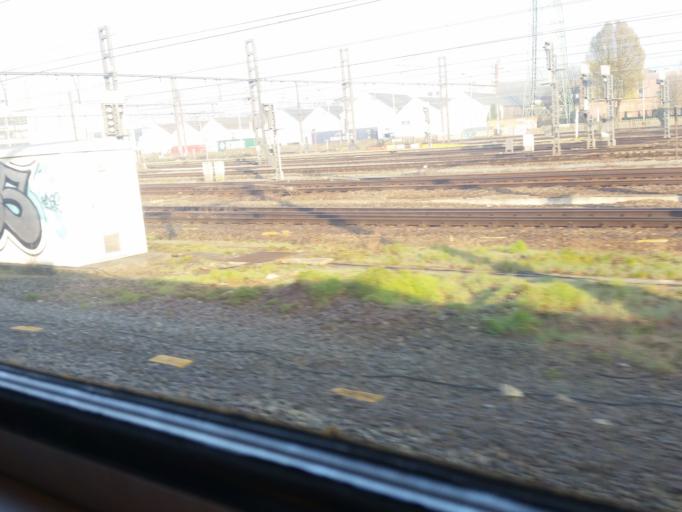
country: BE
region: Brussels Capital
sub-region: Bruxelles-Capitale
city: Brussels
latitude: 50.8797
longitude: 4.3815
